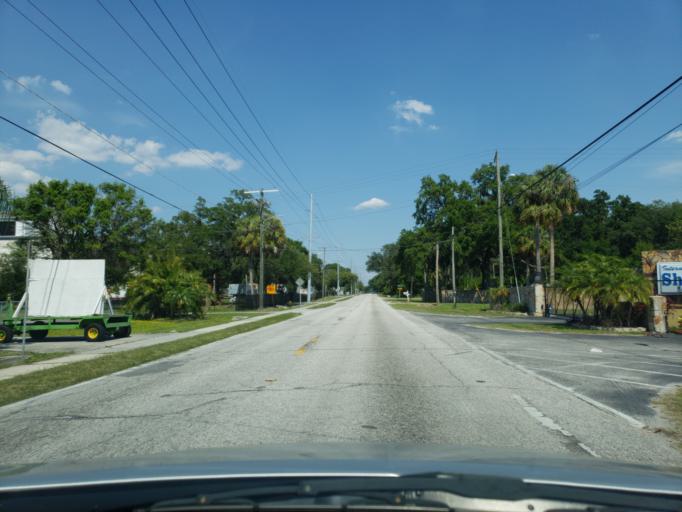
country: US
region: Florida
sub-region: Hillsborough County
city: Gibsonton
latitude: 27.8644
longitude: -82.3782
